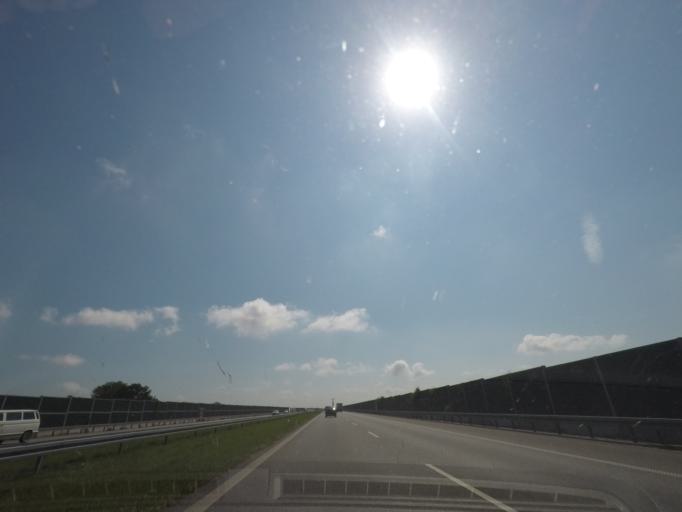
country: PL
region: Kujawsko-Pomorskie
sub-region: Powiat wloclawski
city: Czerniewice
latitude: 52.5284
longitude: 19.0837
